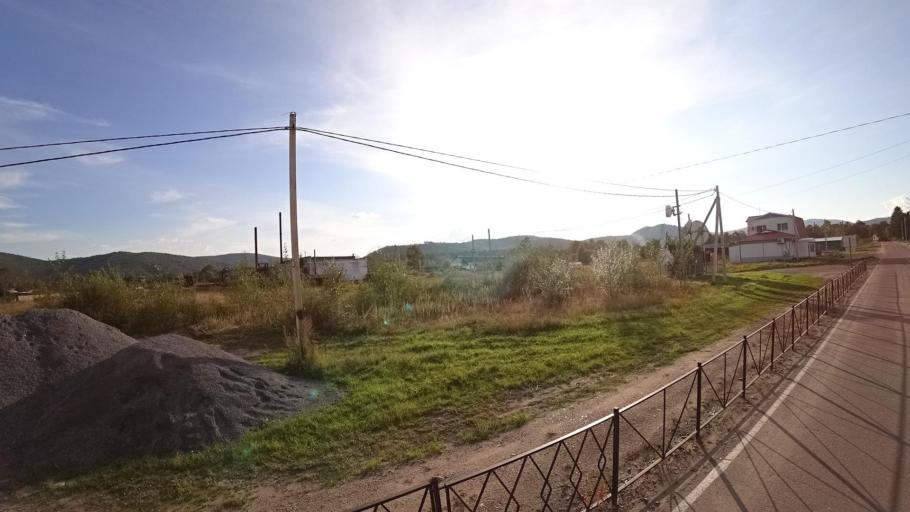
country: RU
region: Jewish Autonomous Oblast
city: Kul'dur
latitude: 49.2017
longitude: 131.6250
